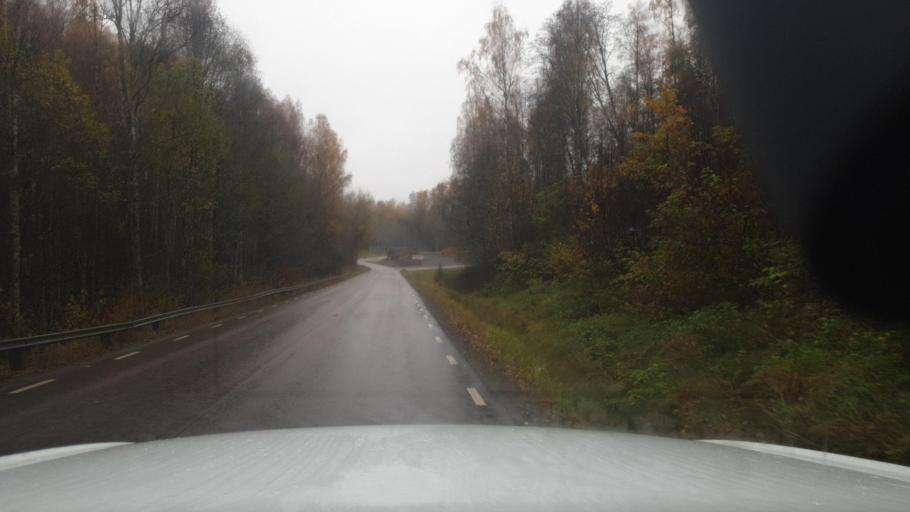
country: SE
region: Vaermland
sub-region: Sunne Kommun
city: Sunne
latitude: 59.7987
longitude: 13.1216
